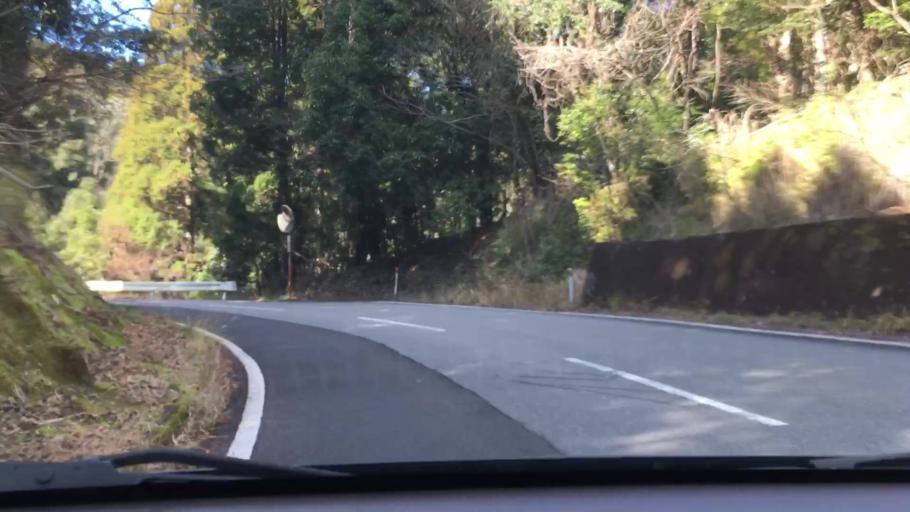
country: JP
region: Kagoshima
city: Ijuin
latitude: 31.7152
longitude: 130.4156
